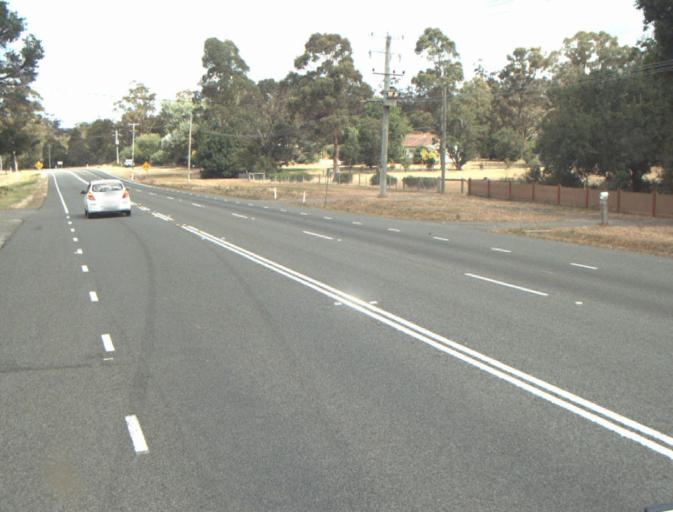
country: AU
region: Tasmania
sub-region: Launceston
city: Mayfield
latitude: -41.2839
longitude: 147.0397
